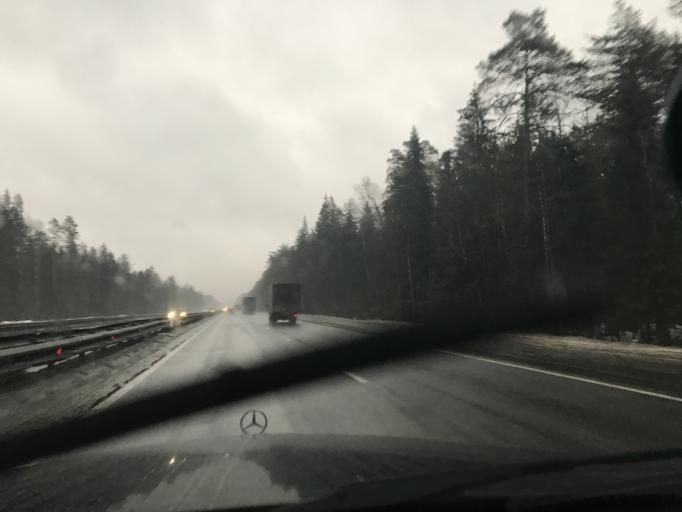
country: RU
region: Vladimir
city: Stepantsevo
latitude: 56.2251
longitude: 41.6141
